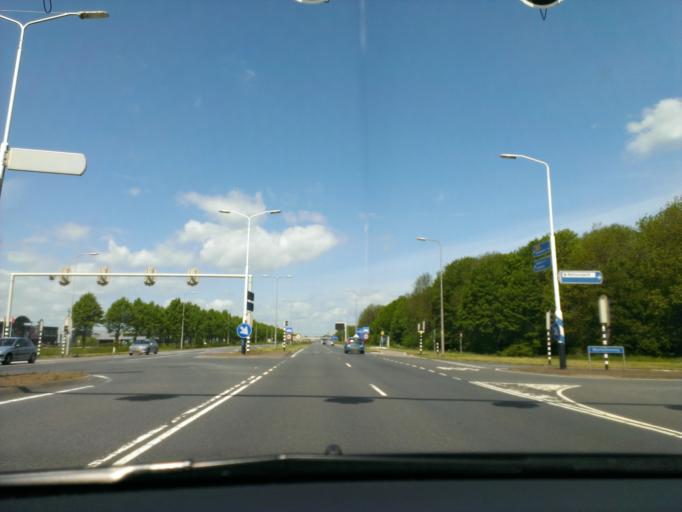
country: NL
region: Flevoland
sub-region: Gemeente Lelystad
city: Lelystad
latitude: 52.4738
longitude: 5.5131
